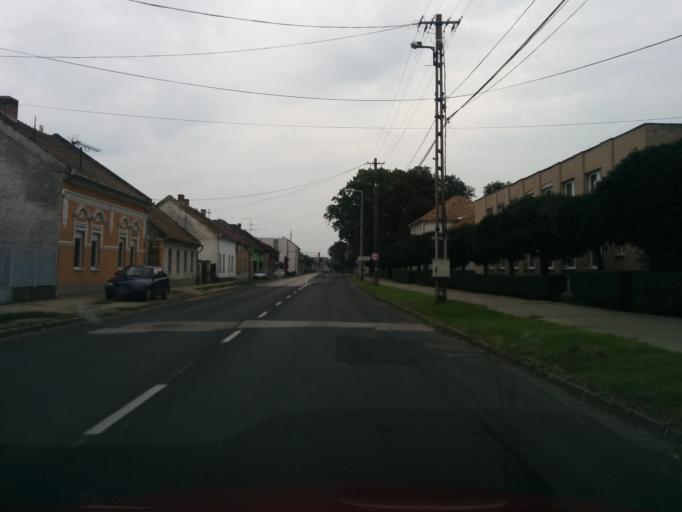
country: HU
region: Komarom-Esztergom
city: Komarom
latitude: 47.7470
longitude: 18.1073
